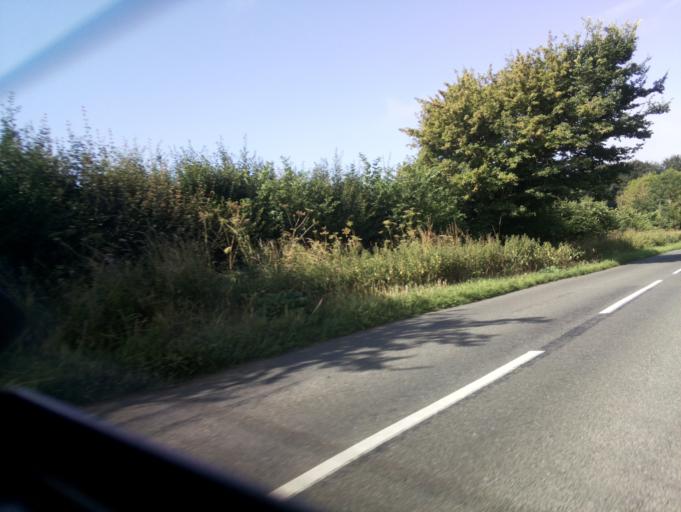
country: GB
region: England
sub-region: Oxfordshire
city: Faringdon
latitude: 51.6499
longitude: -1.6076
